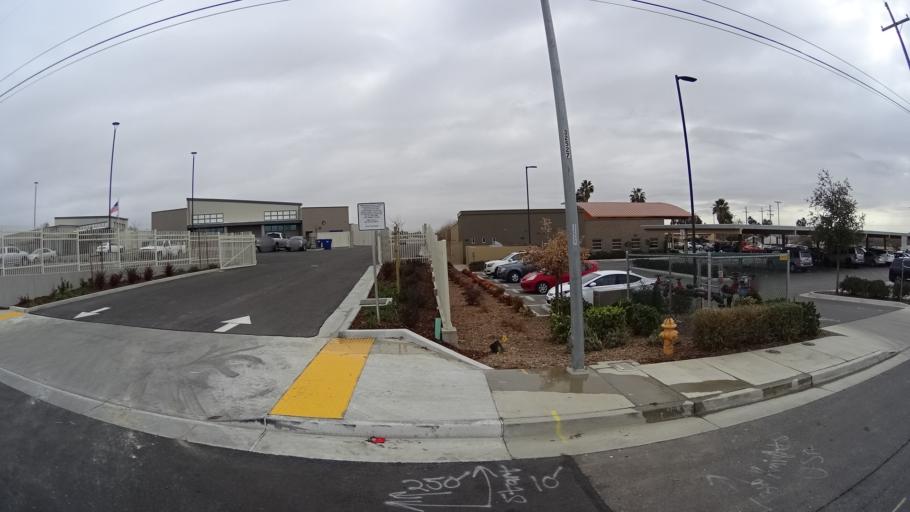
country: US
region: California
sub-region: Kern County
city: Bakersfield
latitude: 35.3771
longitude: -118.9186
